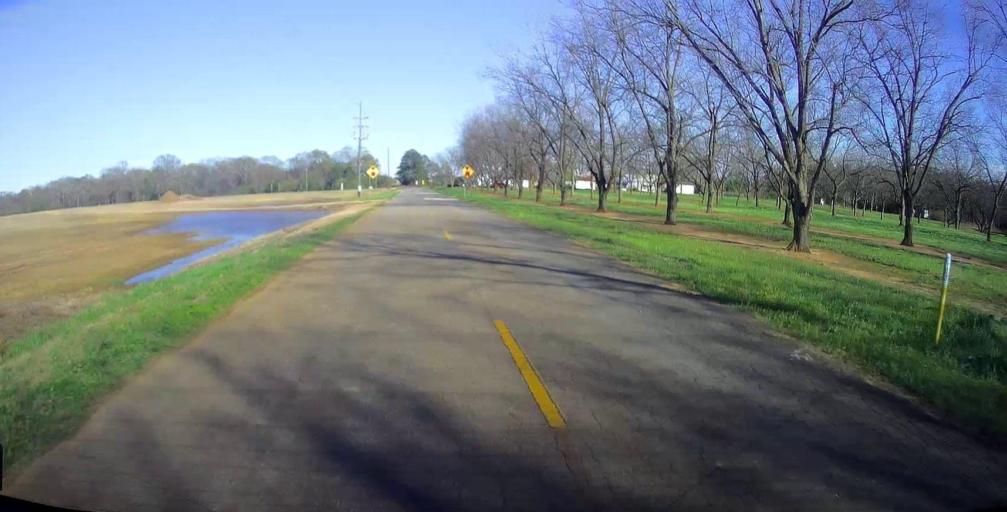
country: US
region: Georgia
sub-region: Macon County
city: Marshallville
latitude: 32.5115
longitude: -83.9264
